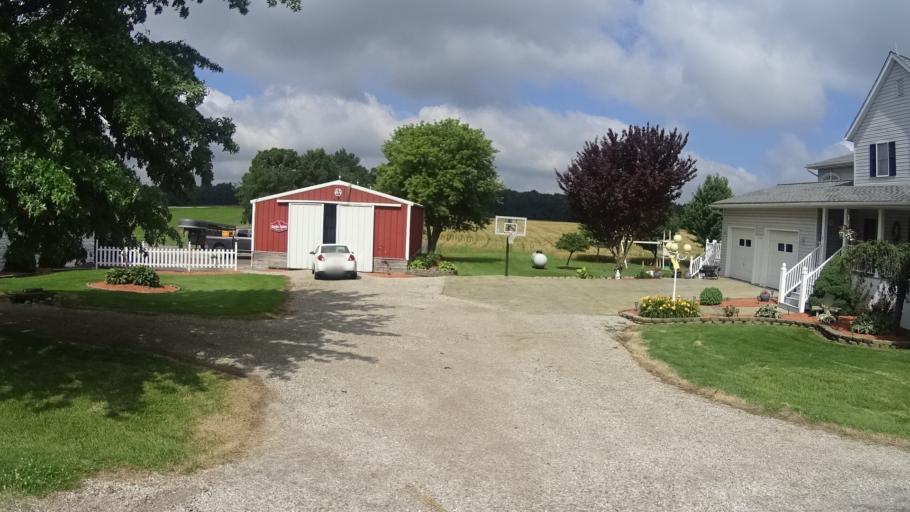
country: US
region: Ohio
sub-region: Huron County
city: Wakeman
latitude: 41.3006
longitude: -82.4133
